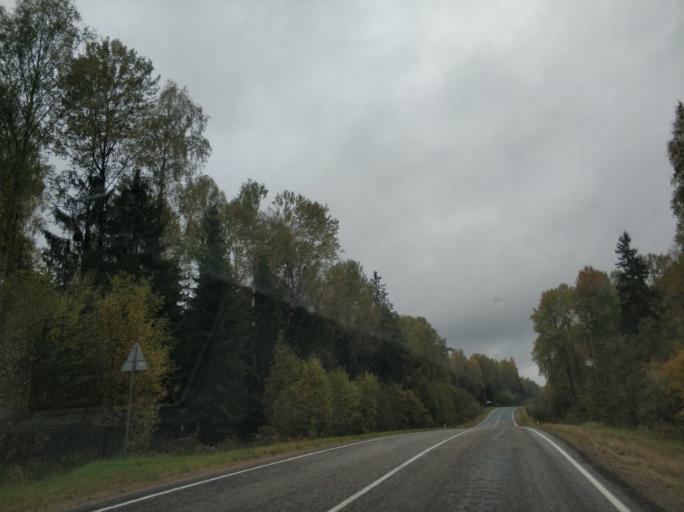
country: RU
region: Pskov
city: Opochka
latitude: 56.5187
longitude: 28.6589
